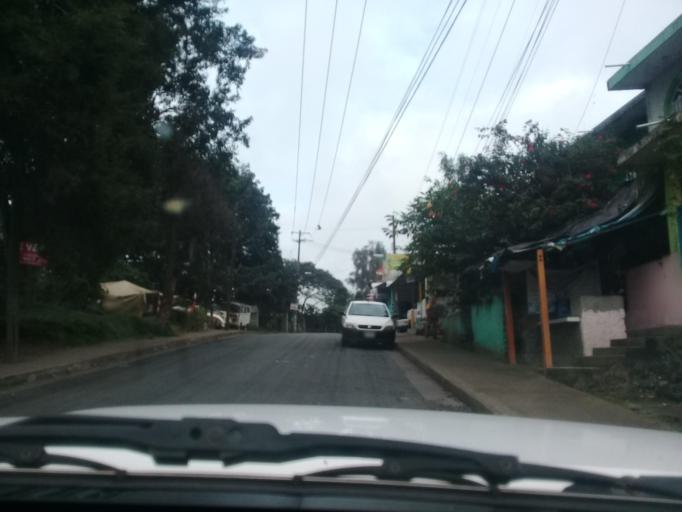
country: MX
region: Veracruz
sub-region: Xalapa
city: Xalapa de Enriquez
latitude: 19.5119
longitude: -96.9093
